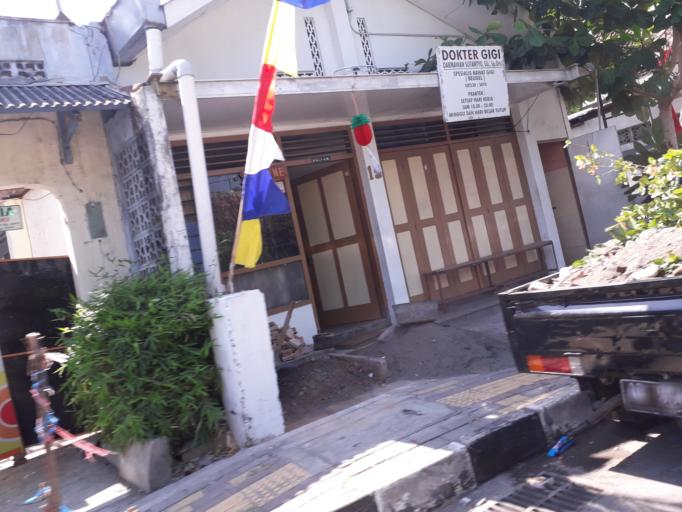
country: ID
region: Daerah Istimewa Yogyakarta
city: Yogyakarta
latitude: -7.7925
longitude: 110.3720
